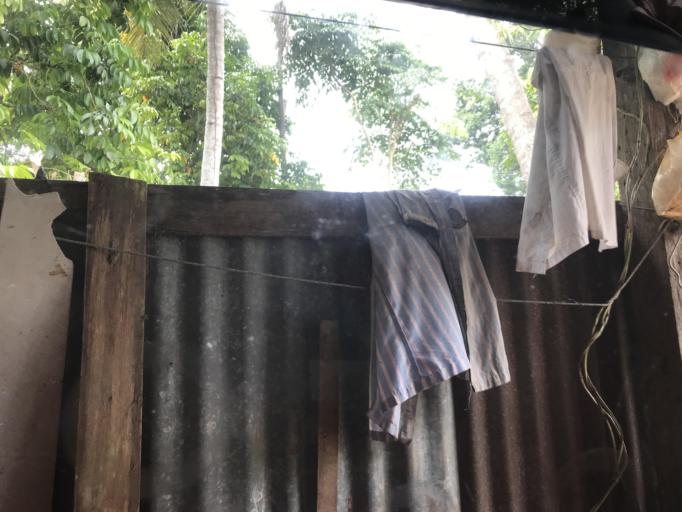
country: MY
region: Kelantan
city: Tumpat
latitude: 6.1656
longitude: 102.2012
